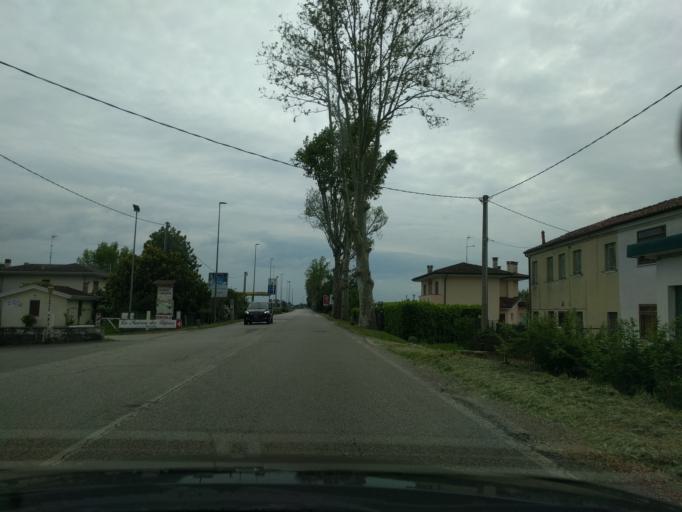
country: IT
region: Veneto
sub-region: Provincia di Rovigo
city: Rovigo
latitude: 45.0421
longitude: 11.7828
